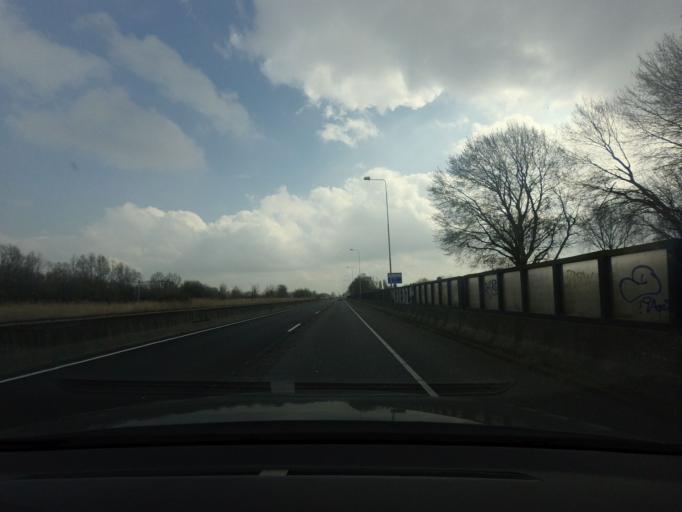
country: NL
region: North Holland
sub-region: Gemeente Zaanstad
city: Zaandam
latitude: 52.3842
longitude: 4.7933
